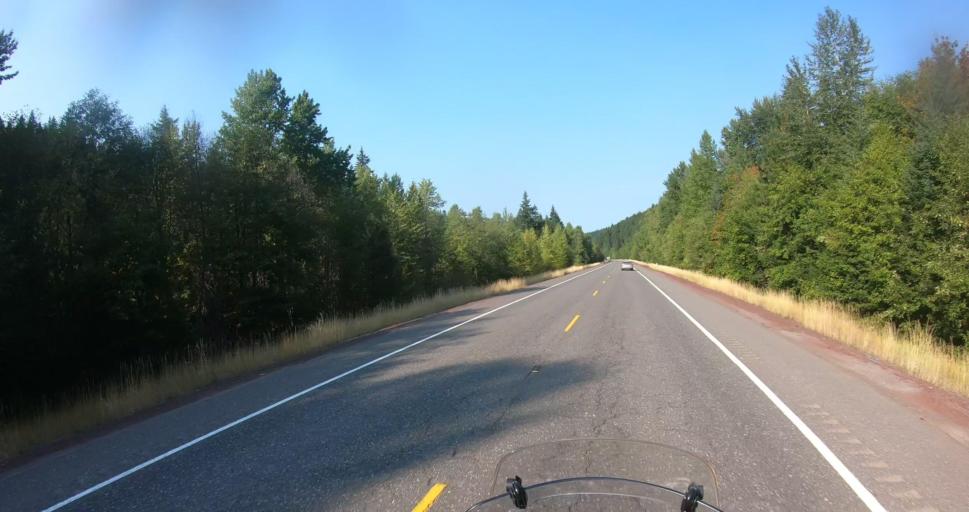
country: US
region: Oregon
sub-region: Hood River County
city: Odell
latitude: 45.4709
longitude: -121.5621
